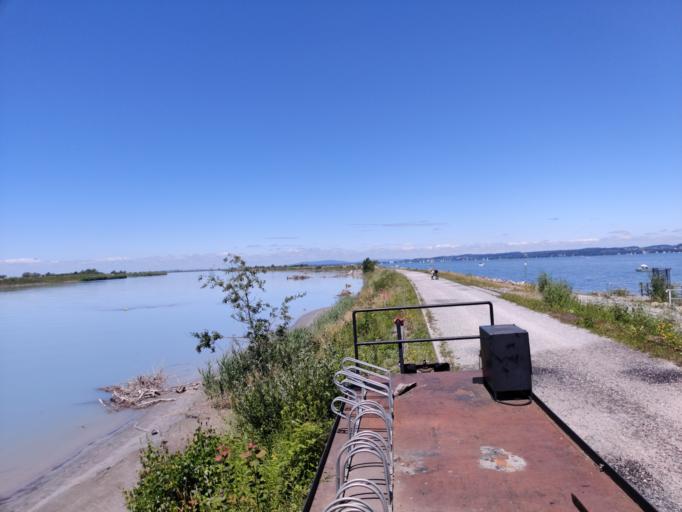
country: AT
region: Vorarlberg
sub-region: Politischer Bezirk Bregenz
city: Hard
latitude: 47.5060
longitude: 9.6696
